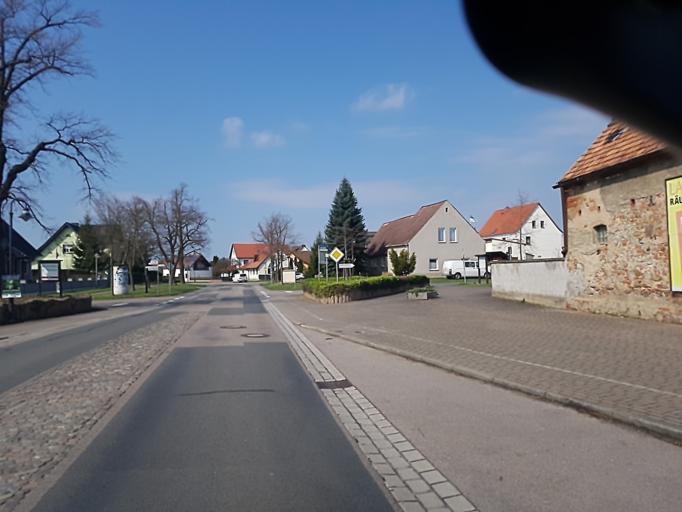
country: DE
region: Saxony
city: Trossin
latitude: 51.5685
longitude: 12.8485
